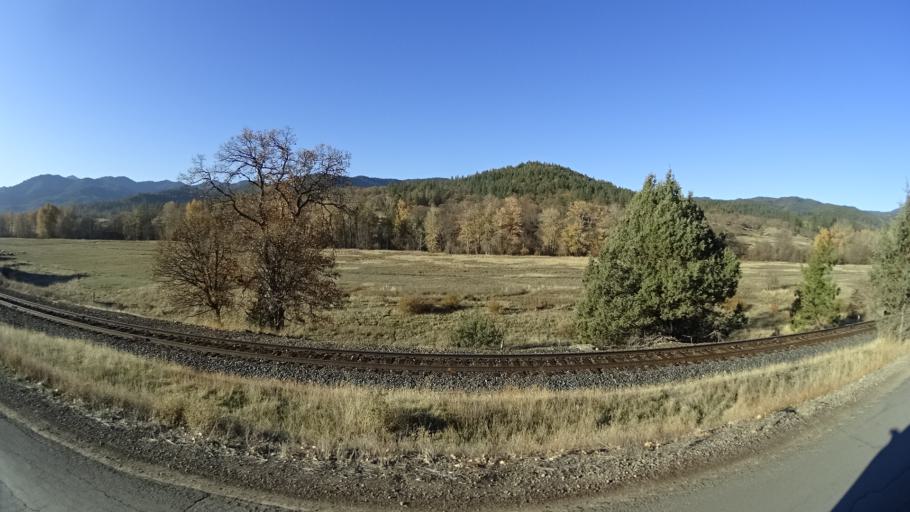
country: US
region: Oregon
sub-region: Jackson County
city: Ashland
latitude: 42.0030
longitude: -122.6422
